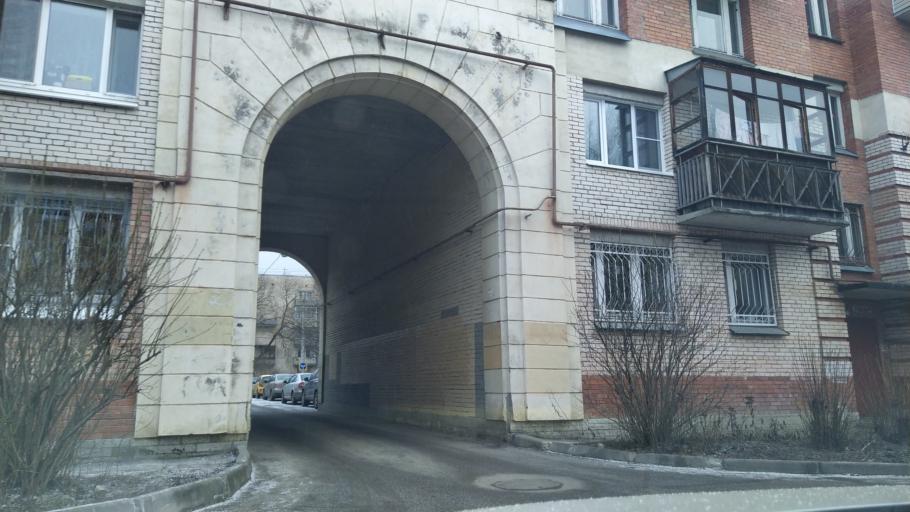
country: RU
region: St.-Petersburg
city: Pushkin
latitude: 59.7264
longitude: 30.4138
